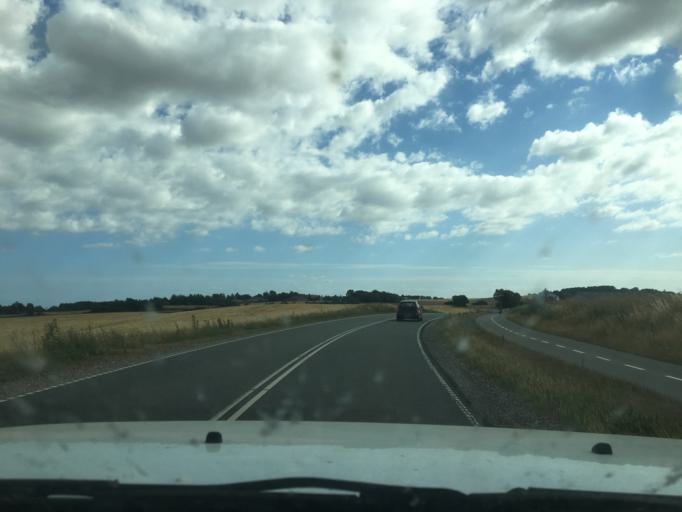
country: DK
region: Central Jutland
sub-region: Arhus Kommune
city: Logten
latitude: 56.2925
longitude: 10.3156
